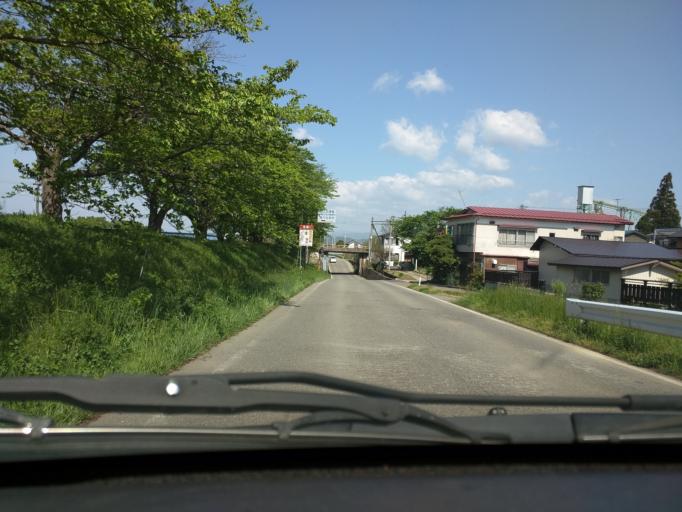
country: JP
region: Fukushima
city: Kitakata
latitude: 37.5913
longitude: 139.8884
